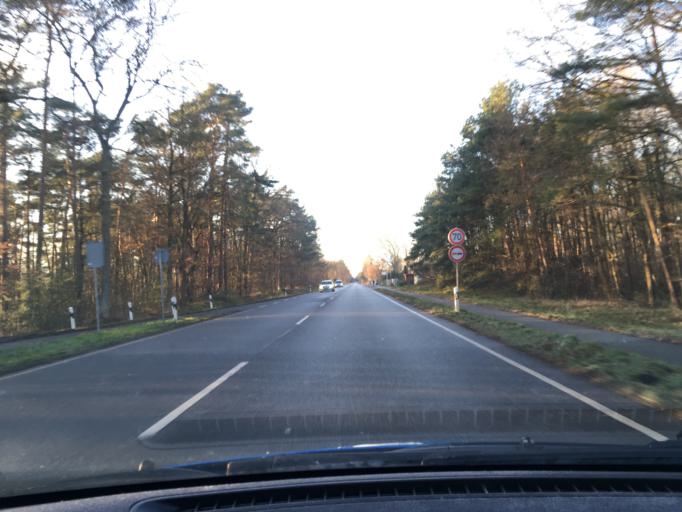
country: DE
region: Lower Saxony
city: Radbruch
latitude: 53.3403
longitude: 10.2810
